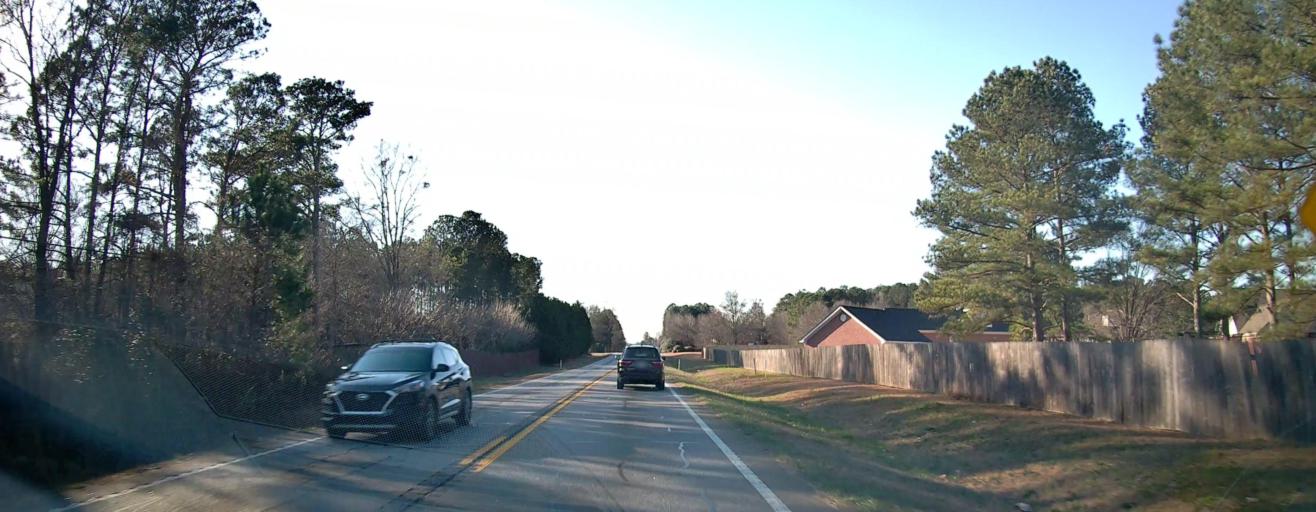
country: US
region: Georgia
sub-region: Henry County
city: Hampton
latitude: 33.4219
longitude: -84.2691
